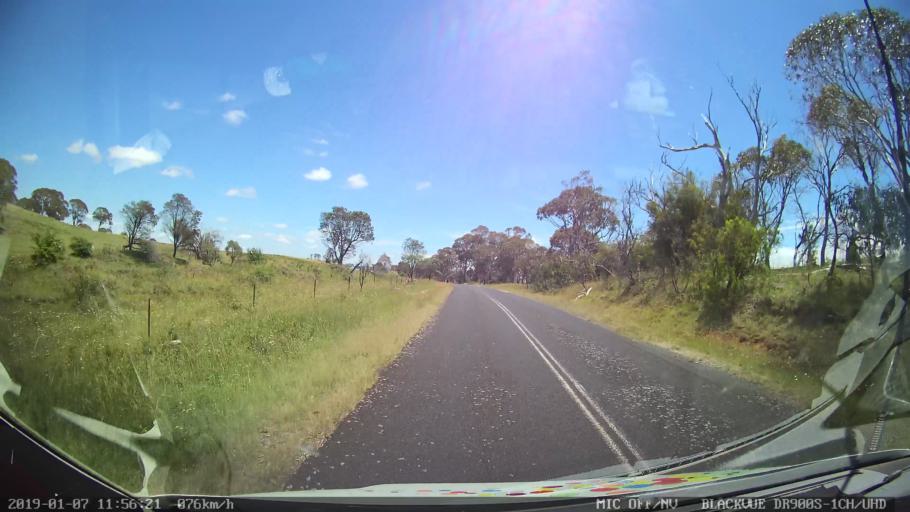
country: AU
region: New South Wales
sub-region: Guyra
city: Guyra
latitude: -30.2755
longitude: 151.6739
